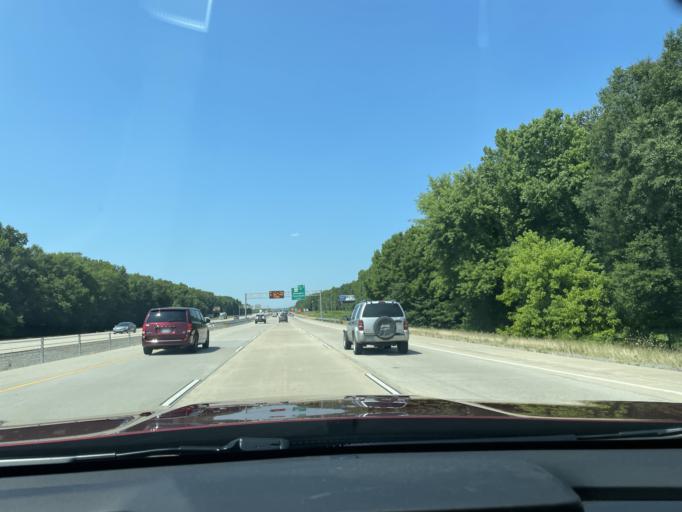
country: US
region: Arkansas
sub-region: Pulaski County
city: Jacksonville
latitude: 34.8559
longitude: -92.1355
